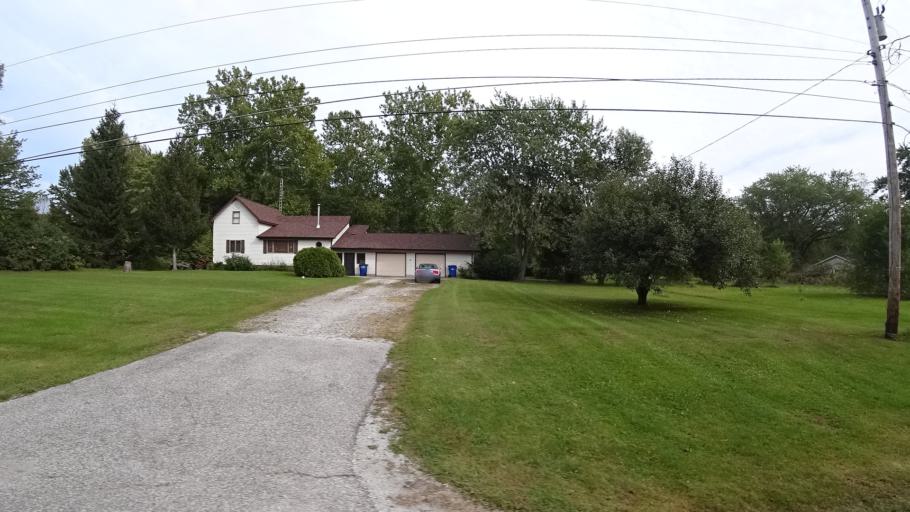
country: US
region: Indiana
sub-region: LaPorte County
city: Long Beach
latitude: 41.7245
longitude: -86.8162
